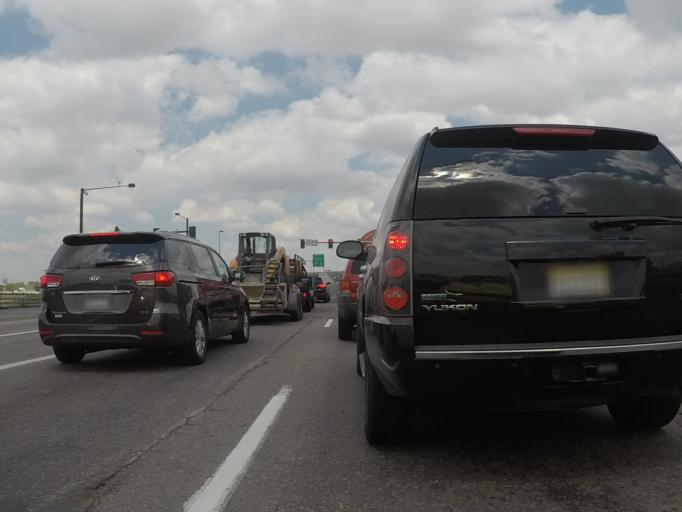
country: US
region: Colorado
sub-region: Adams County
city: Commerce City
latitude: 39.7814
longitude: -104.9021
